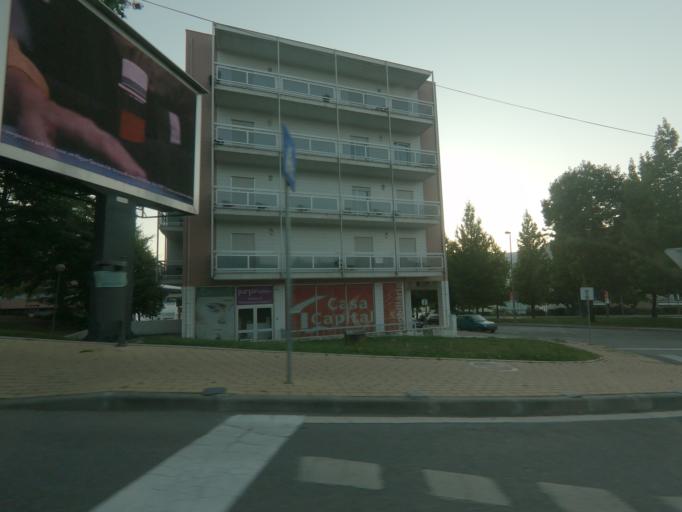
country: PT
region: Vila Real
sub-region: Vila Real
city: Vila Real
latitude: 41.2988
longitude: -7.7323
